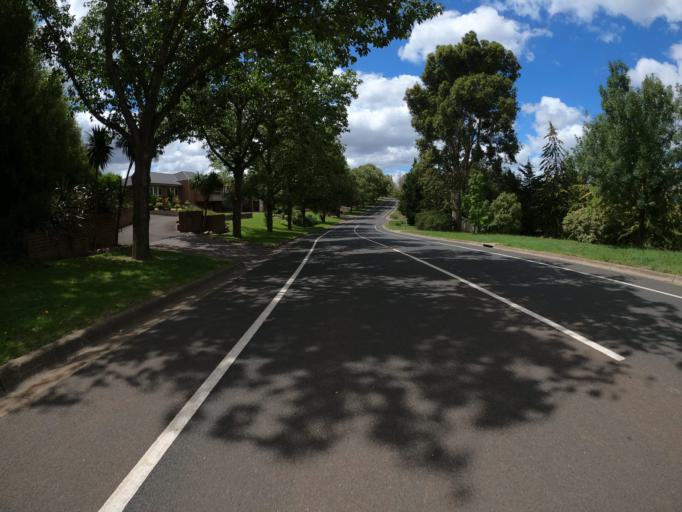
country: AU
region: Victoria
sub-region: Hume
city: Attwood
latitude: -37.6575
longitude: 144.8953
